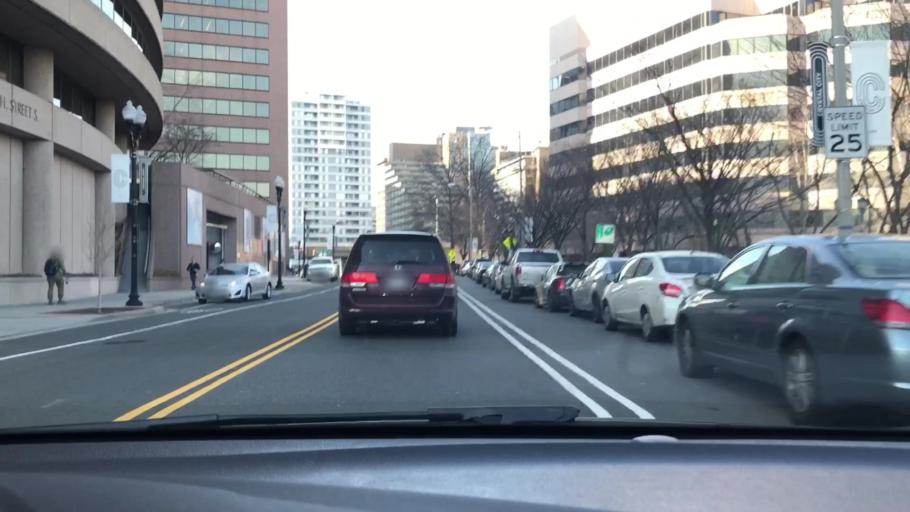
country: US
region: Washington, D.C.
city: Washington, D.C.
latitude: 38.8626
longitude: -77.0492
